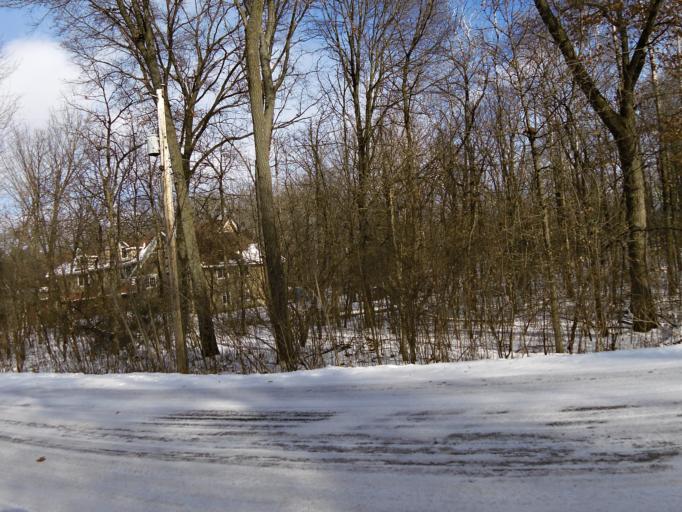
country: US
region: Minnesota
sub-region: Washington County
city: Lake Elmo
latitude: 44.9694
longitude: -92.8348
